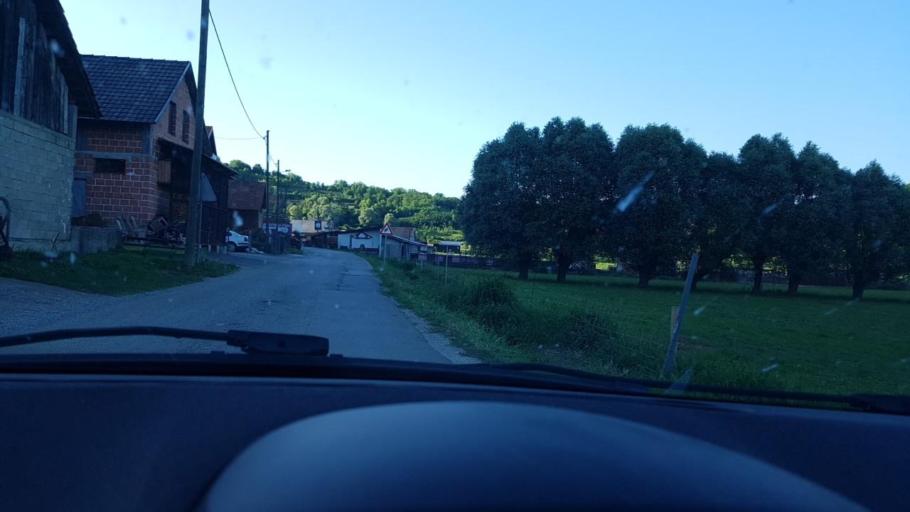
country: HR
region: Krapinsko-Zagorska
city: Mihovljan
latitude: 46.0894
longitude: 15.9365
